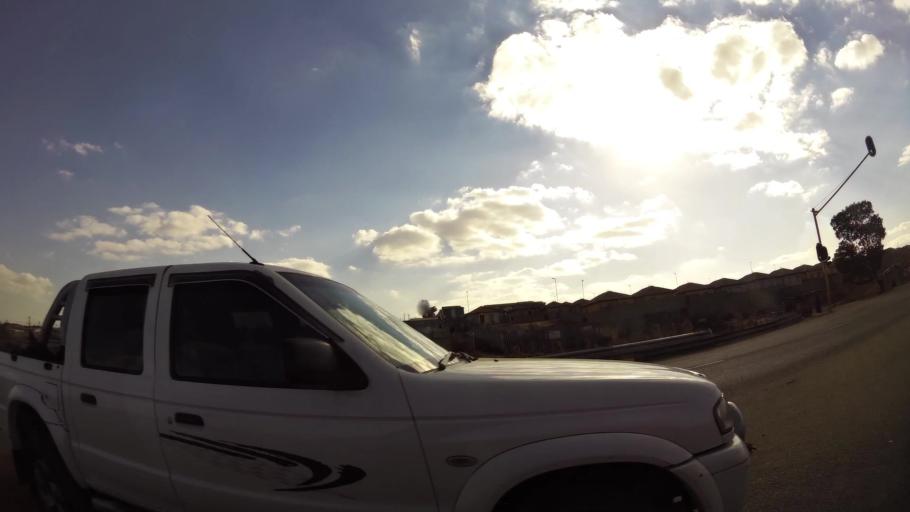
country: ZA
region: Gauteng
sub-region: Ekurhuleni Metropolitan Municipality
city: Tembisa
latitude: -25.9847
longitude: 28.1931
